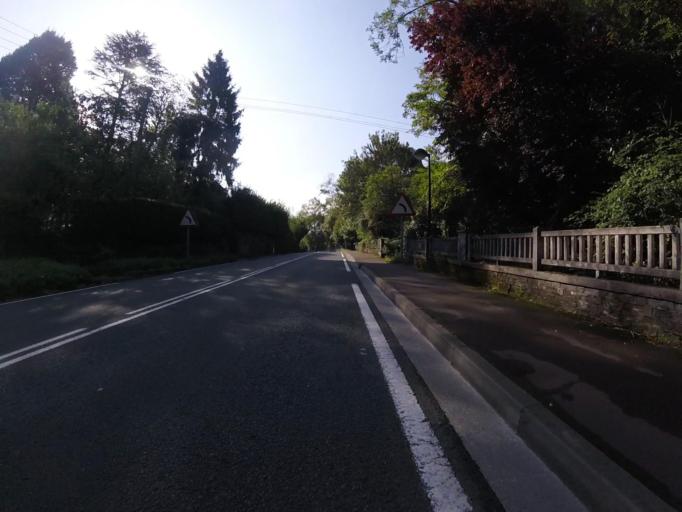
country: ES
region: Basque Country
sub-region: Provincia de Guipuzcoa
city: Lezo
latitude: 43.3018
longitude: -1.8673
